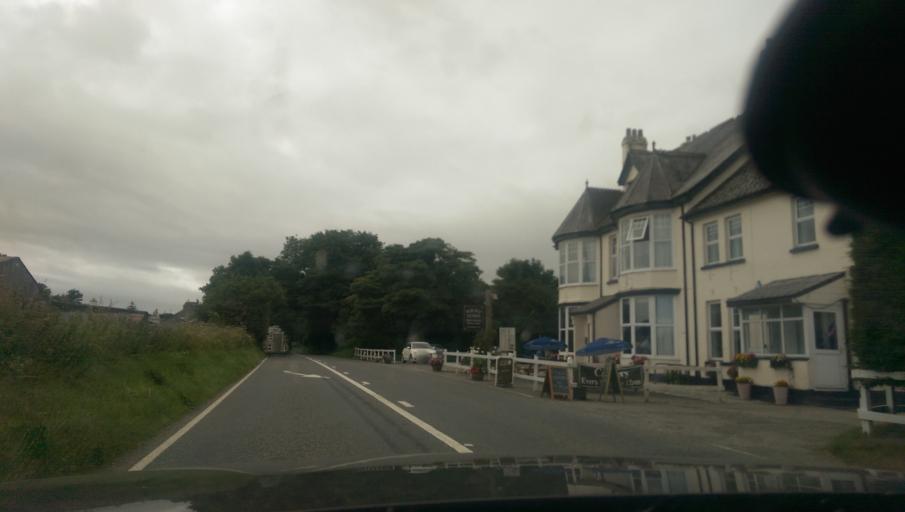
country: GB
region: England
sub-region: Cornwall
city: Jacobstow
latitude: 50.6616
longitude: -4.5744
